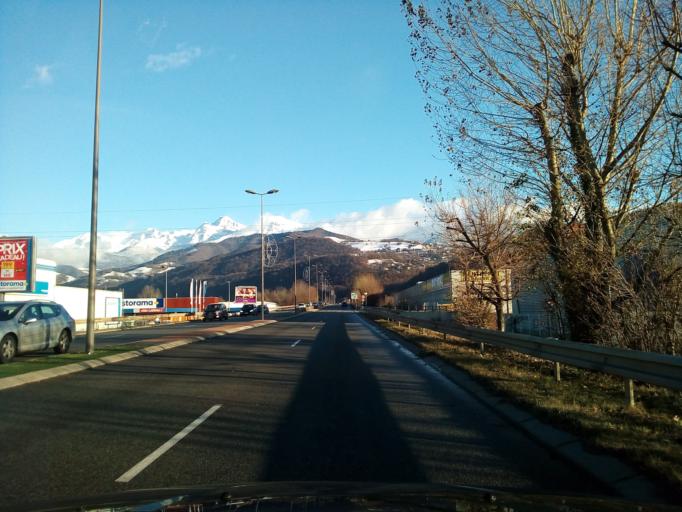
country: FR
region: Rhone-Alpes
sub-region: Departement de l'Isere
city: Saint-Martin-d'Heres
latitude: 45.1837
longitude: 5.7707
